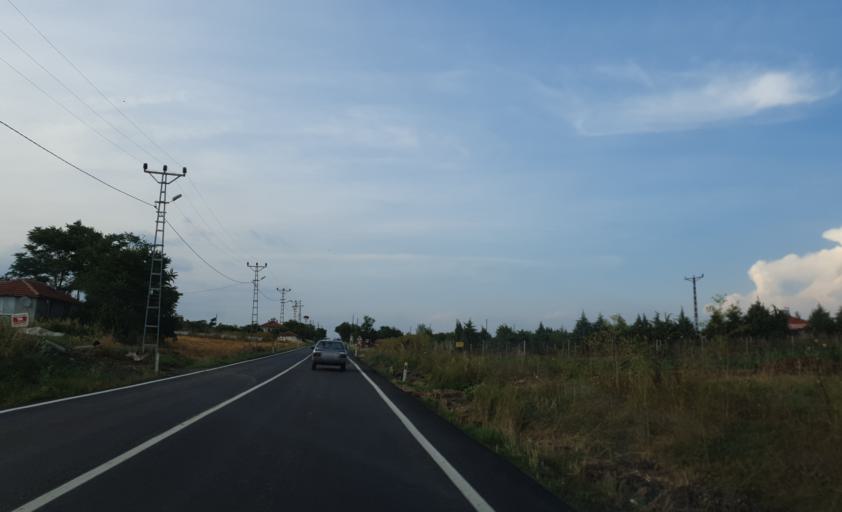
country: TR
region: Tekirdag
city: Hayrabolu
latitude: 41.2887
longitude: 27.1332
